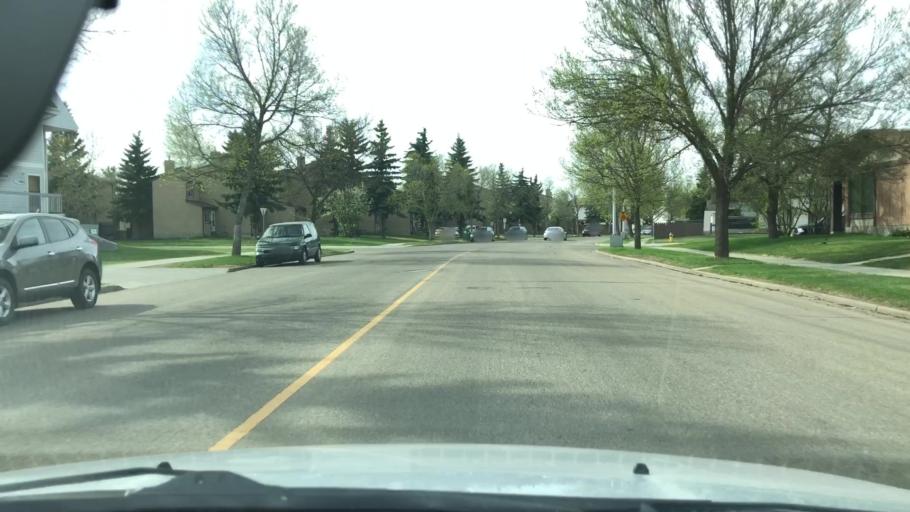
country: CA
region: Alberta
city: Edmonton
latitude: 53.6019
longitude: -113.5290
